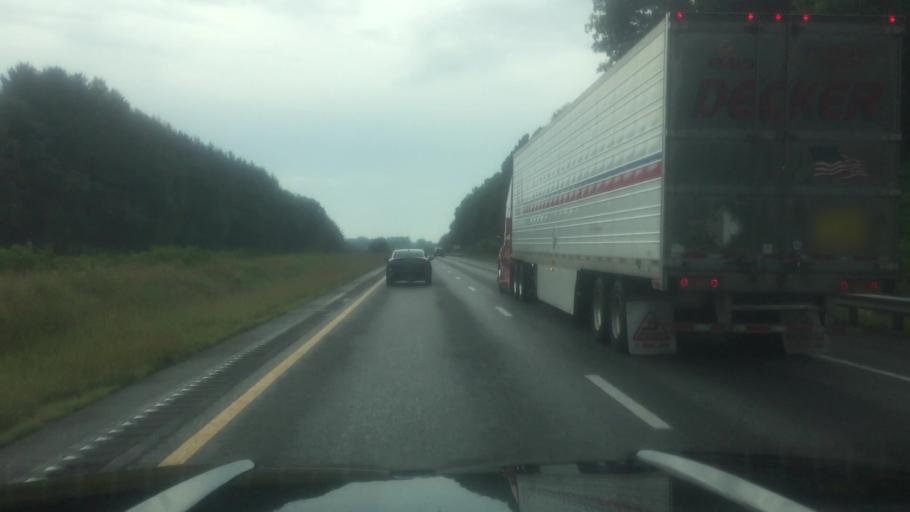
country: US
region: Virginia
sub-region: Carroll County
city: Hillsville
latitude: 36.7093
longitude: -80.7424
